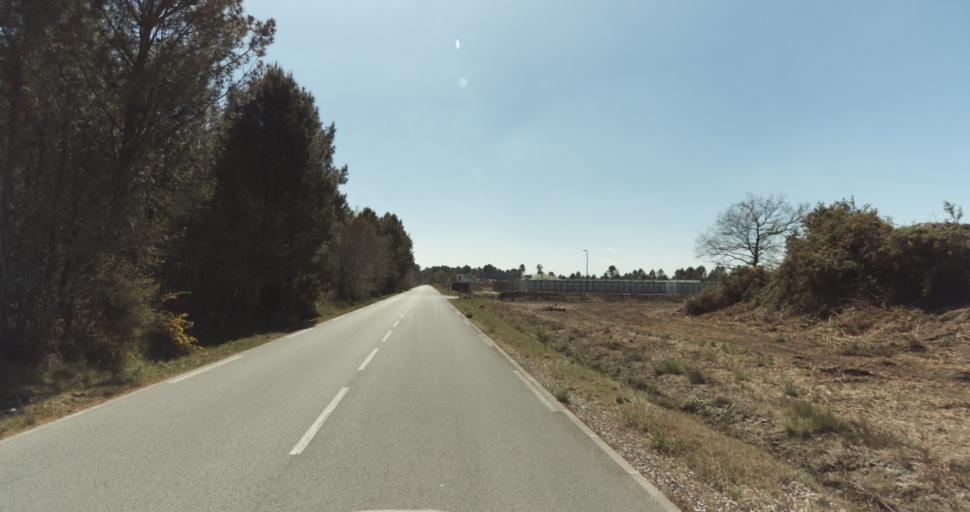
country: FR
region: Aquitaine
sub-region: Departement de la Gironde
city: Martignas-sur-Jalle
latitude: 44.8075
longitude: -0.7523
